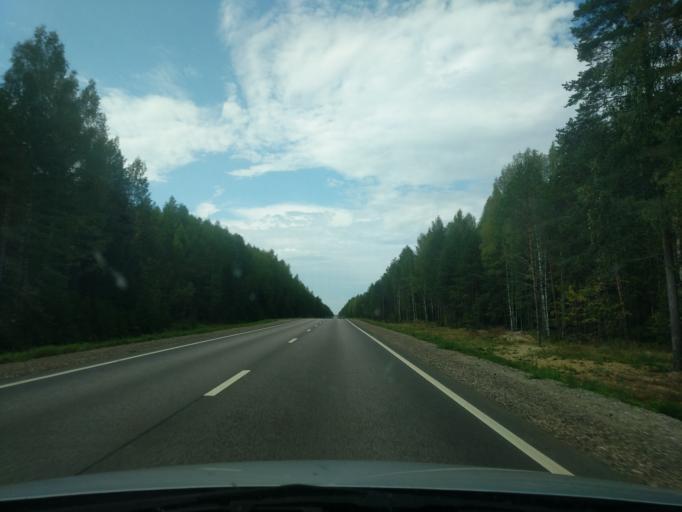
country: RU
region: Kostroma
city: Kadyy
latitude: 57.7944
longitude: 42.9600
